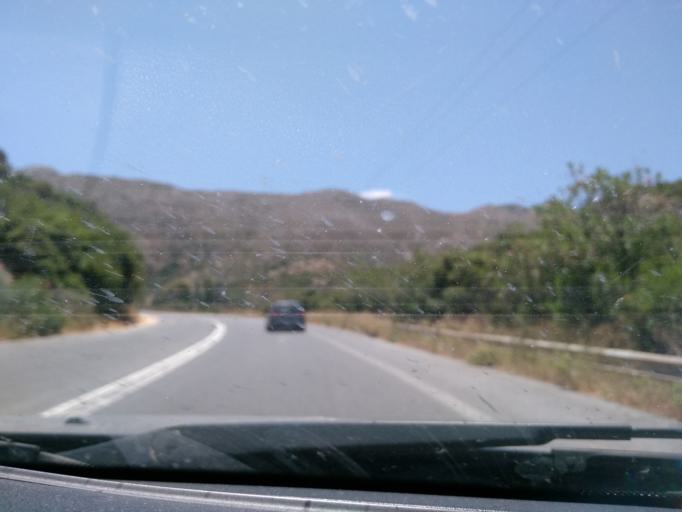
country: GR
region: Crete
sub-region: Nomos Rethymnis
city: Anogeia
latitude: 35.3870
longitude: 24.9195
